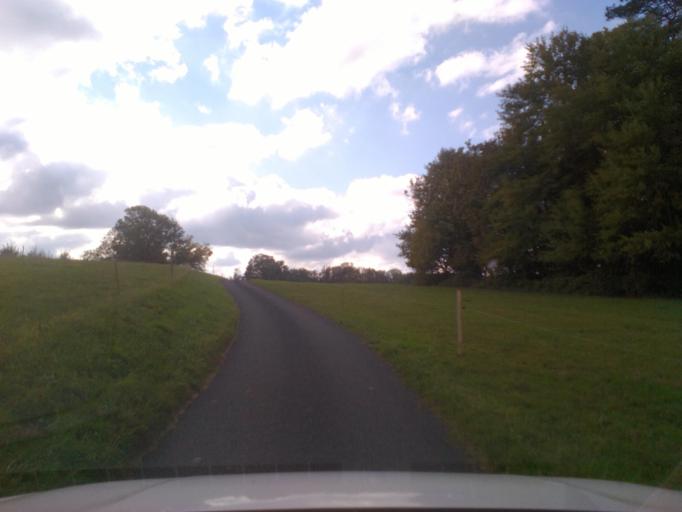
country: FR
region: Lorraine
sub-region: Departement des Vosges
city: Senones
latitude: 48.3493
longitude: 7.0176
